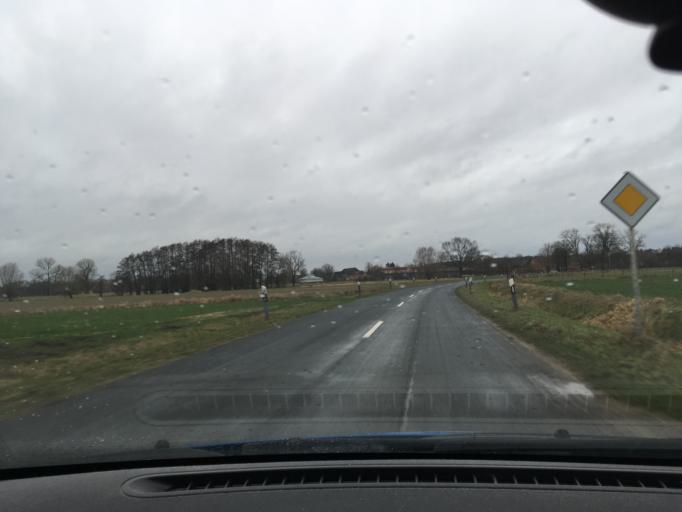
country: DE
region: Schleswig-Holstein
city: Lanze
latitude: 53.3638
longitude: 10.6371
